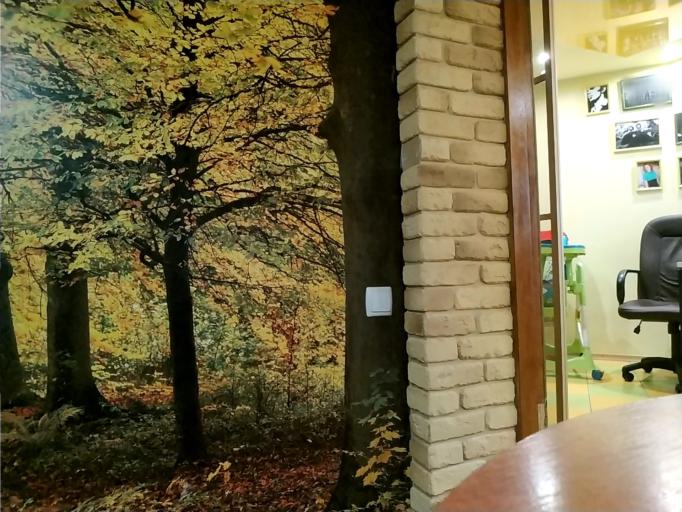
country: RU
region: Tverskaya
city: Staraya Toropa
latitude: 56.3396
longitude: 31.8557
